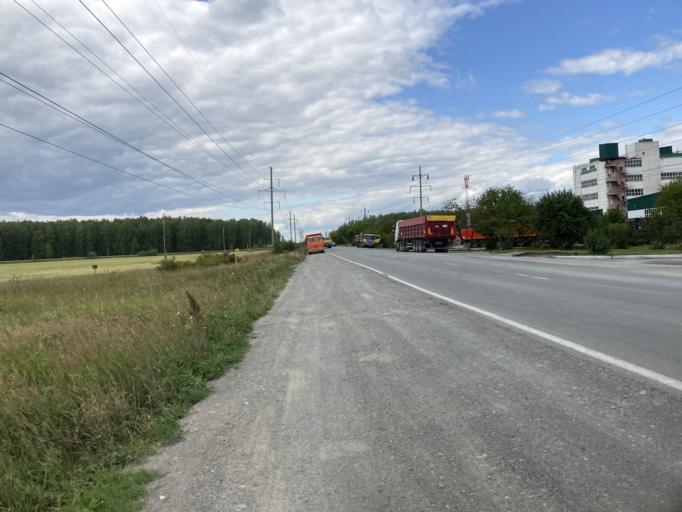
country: RU
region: Sverdlovsk
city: Bogdanovich
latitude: 56.8045
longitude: 62.0354
